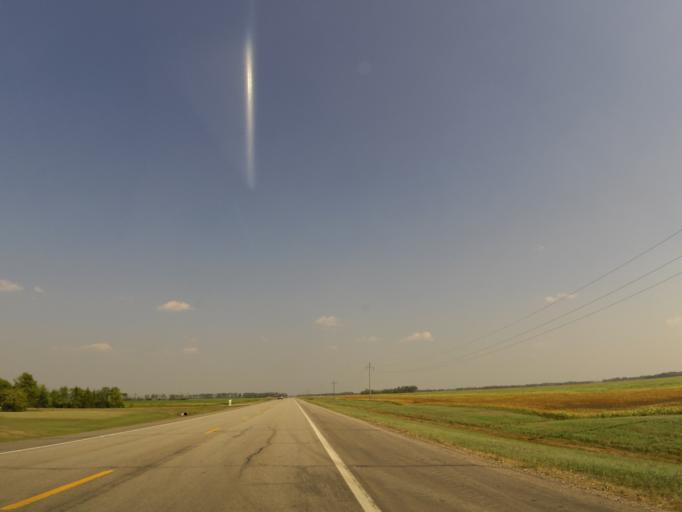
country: US
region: North Dakota
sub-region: Walsh County
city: Grafton
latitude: 48.4119
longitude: -97.2563
